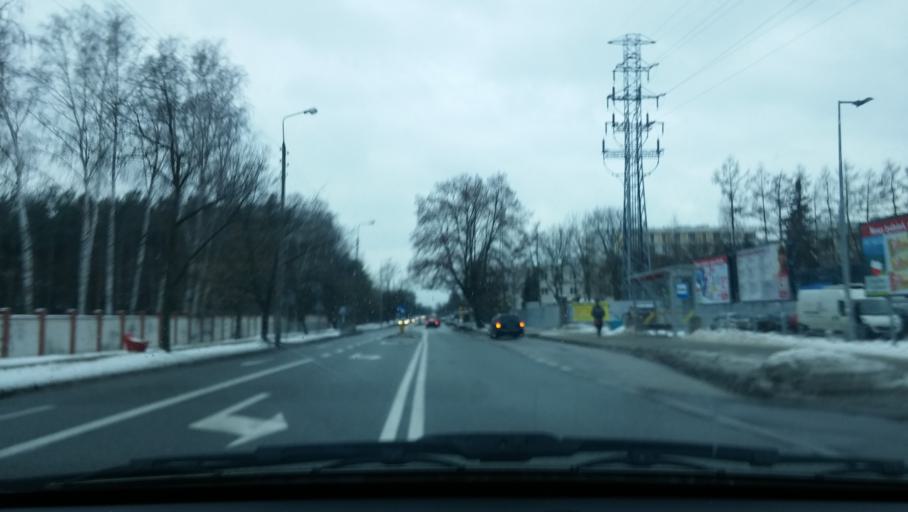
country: PL
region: Masovian Voivodeship
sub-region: Warszawa
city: Rembertow
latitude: 52.2412
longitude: 21.1621
